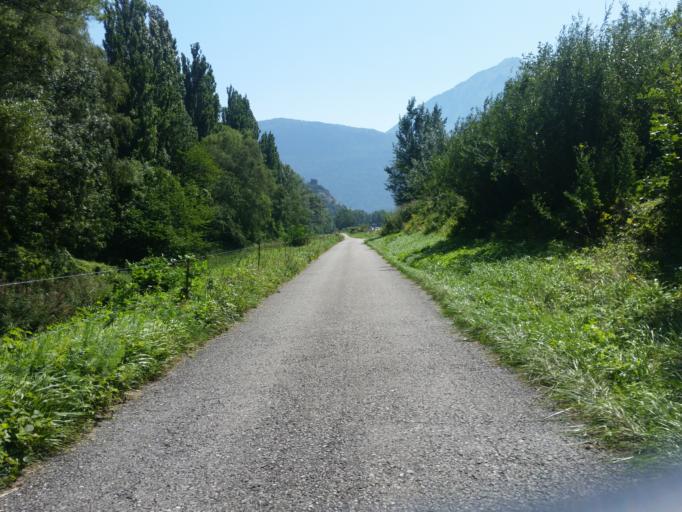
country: CH
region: Valais
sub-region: Saint-Maurice District
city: Vernayaz
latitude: 46.1331
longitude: 7.0556
